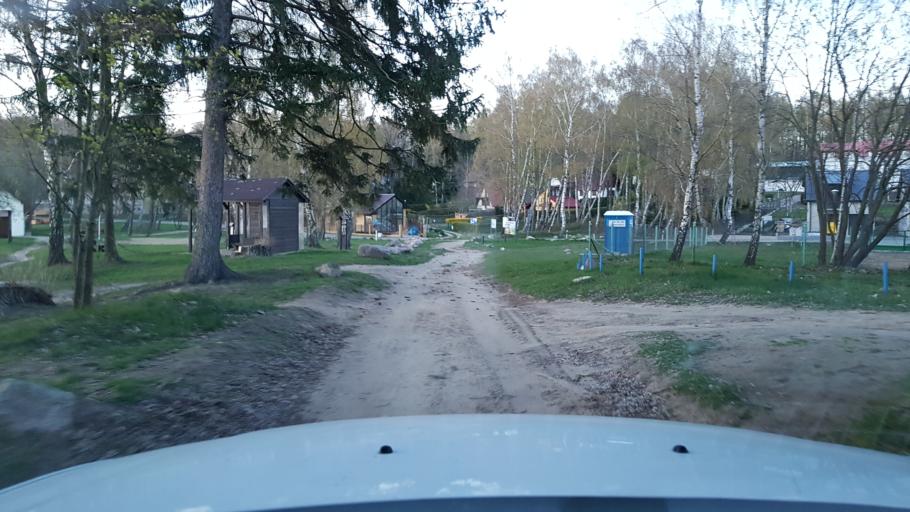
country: PL
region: West Pomeranian Voivodeship
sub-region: Powiat stargardzki
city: Insko
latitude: 53.4459
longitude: 15.5606
